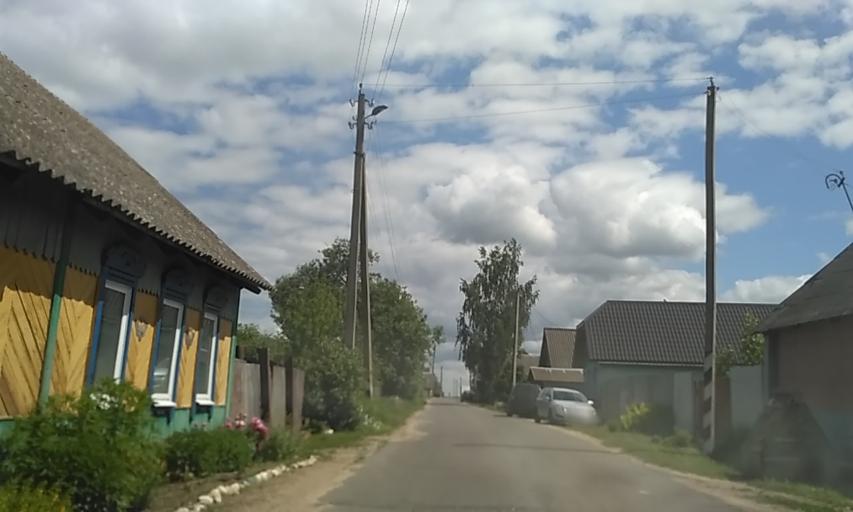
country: BY
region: Minsk
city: Krupki
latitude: 54.3490
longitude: 29.1307
